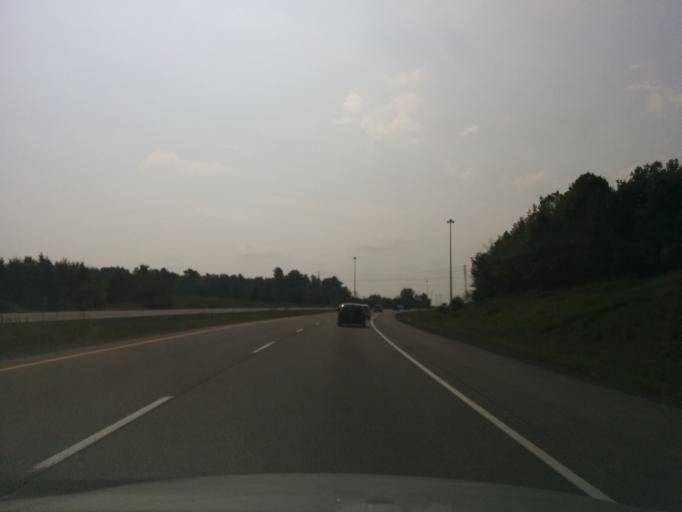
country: CA
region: Ontario
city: Bells Corners
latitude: 45.3258
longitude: -75.8064
